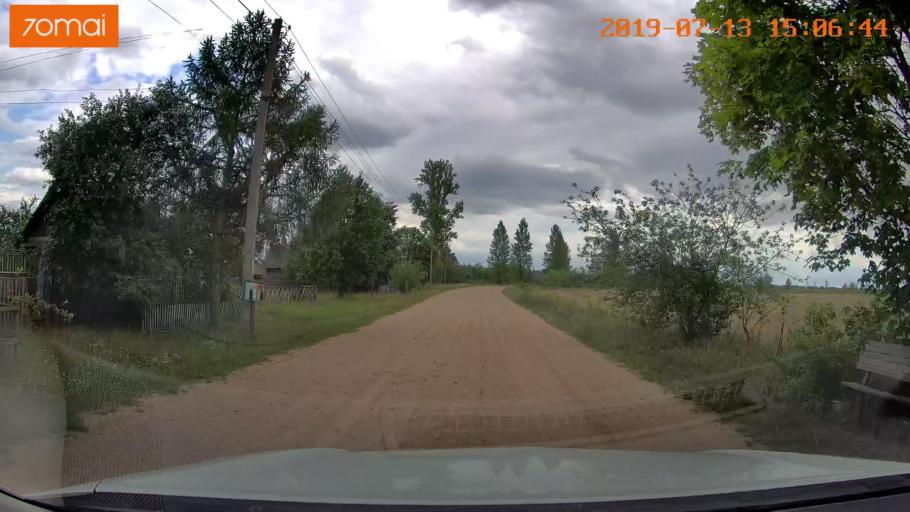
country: BY
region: Mogilev
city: Hlusha
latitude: 53.1964
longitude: 28.7558
